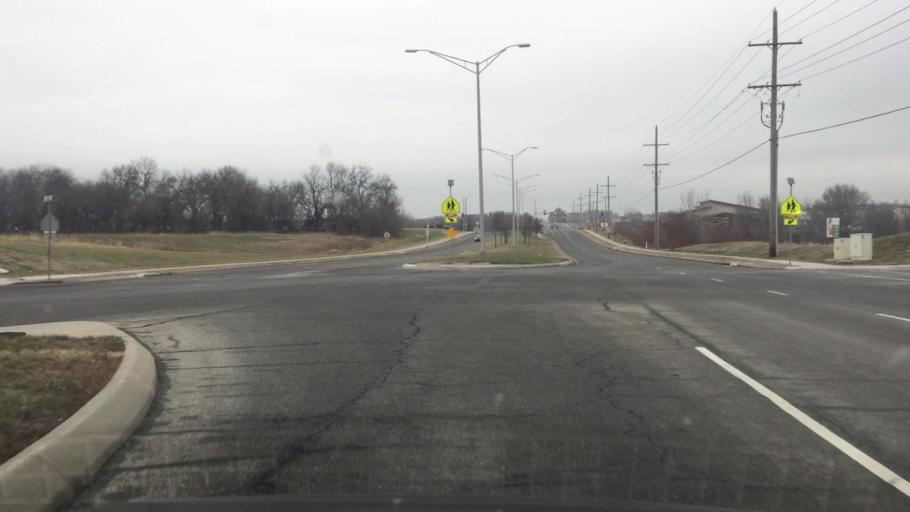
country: US
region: Kansas
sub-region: Johnson County
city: Lenexa
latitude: 38.8306
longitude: -94.6863
